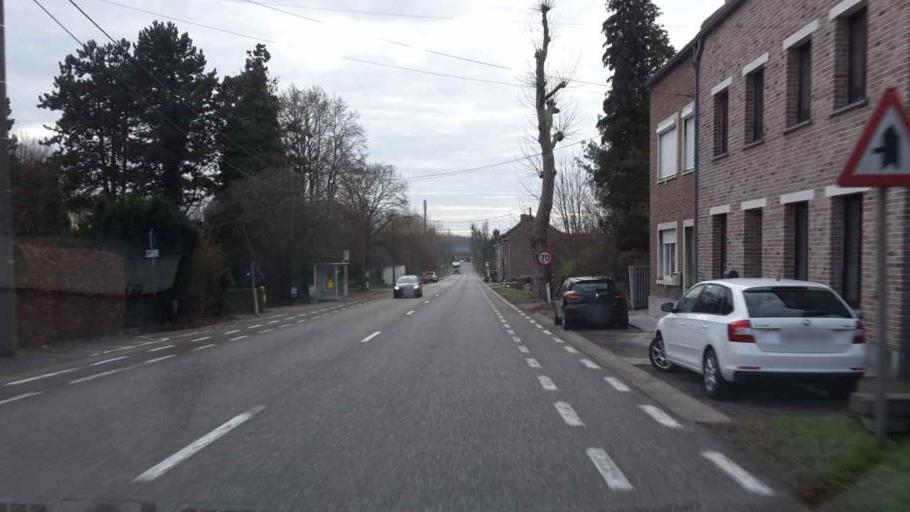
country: BE
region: Flanders
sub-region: Provincie Vlaams-Brabant
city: Tienen
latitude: 50.7924
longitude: 4.9145
